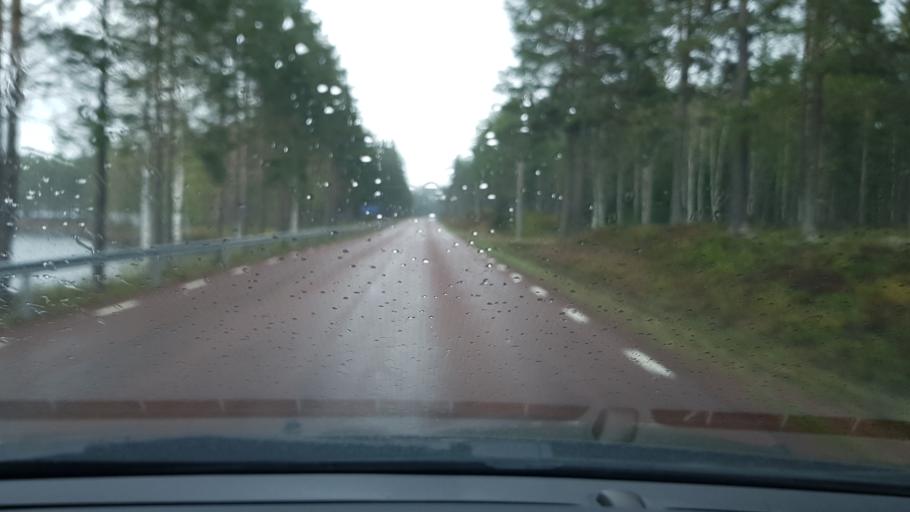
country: SE
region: Dalarna
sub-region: Alvdalens Kommun
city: AElvdalen
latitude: 61.1180
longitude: 14.1383
